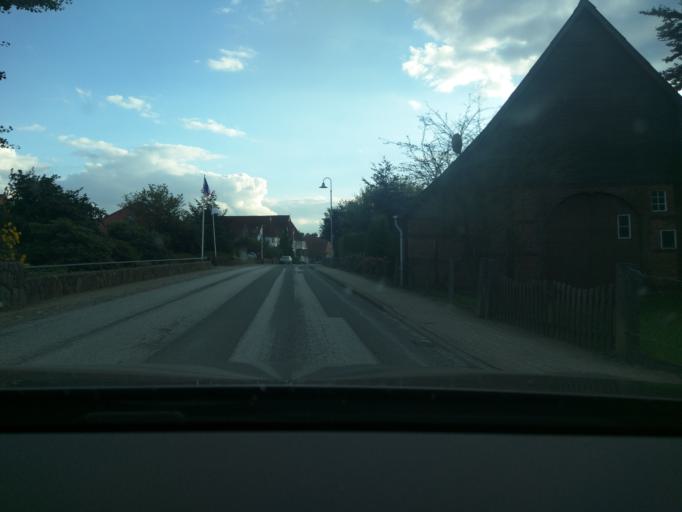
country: DE
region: Schleswig-Holstein
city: Lutau
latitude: 53.4337
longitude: 10.5485
